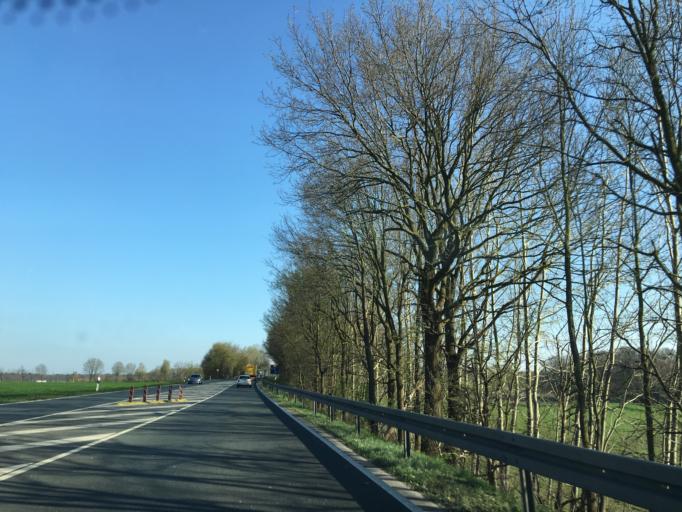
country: DE
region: North Rhine-Westphalia
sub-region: Regierungsbezirk Munster
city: Greven
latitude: 52.0886
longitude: 7.6380
